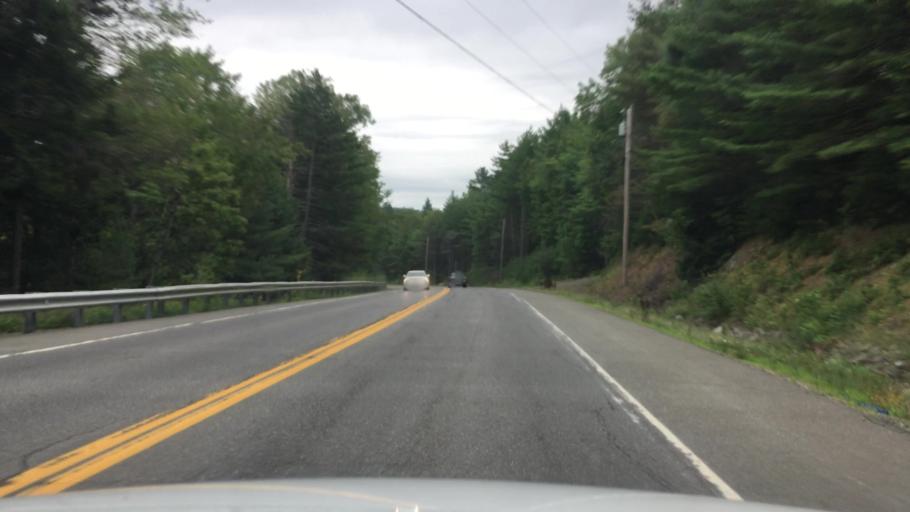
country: US
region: Maine
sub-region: Penobscot County
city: Bradley
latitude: 44.8252
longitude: -68.4102
